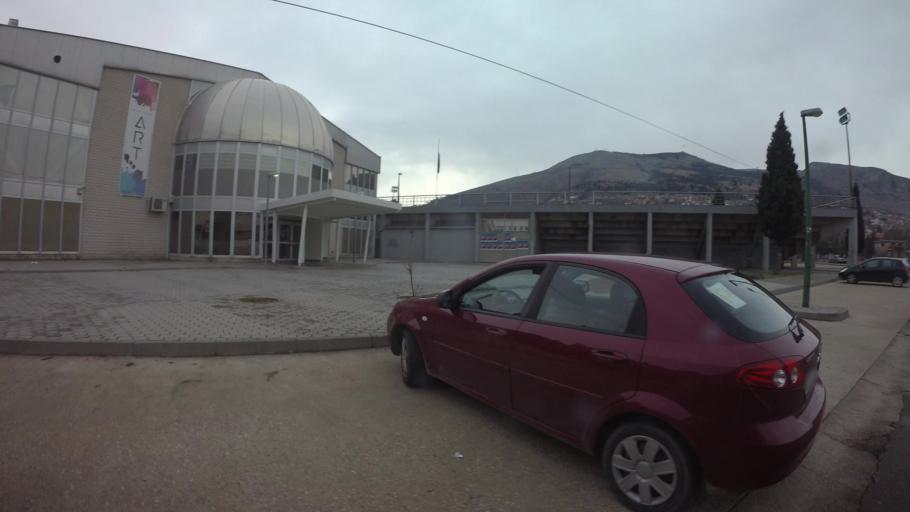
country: BA
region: Federation of Bosnia and Herzegovina
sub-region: Hercegovacko-Bosanski Kanton
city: Mostar
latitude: 43.3543
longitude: 17.8081
